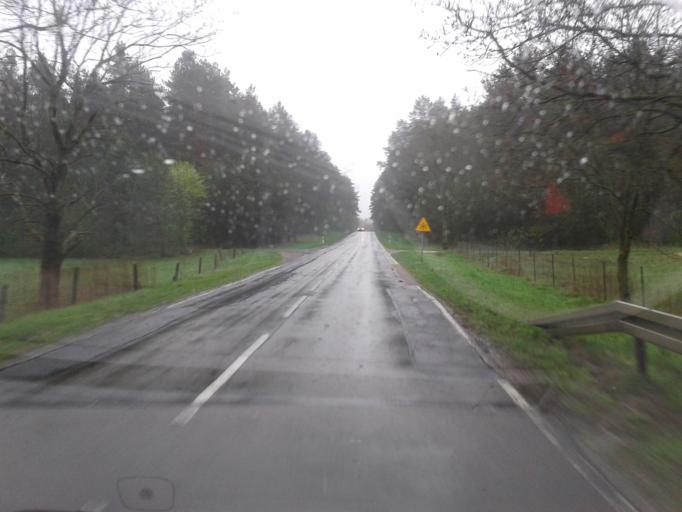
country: PL
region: Subcarpathian Voivodeship
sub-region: Powiat lubaczowski
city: Cieszanow
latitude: 50.2714
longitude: 23.1499
